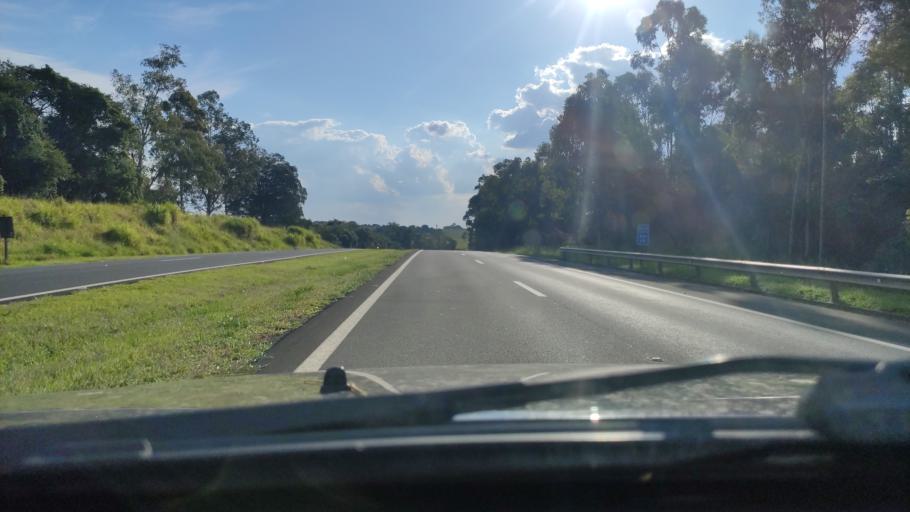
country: BR
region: Sao Paulo
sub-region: Itapira
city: Itapira
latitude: -22.4530
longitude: -46.8683
